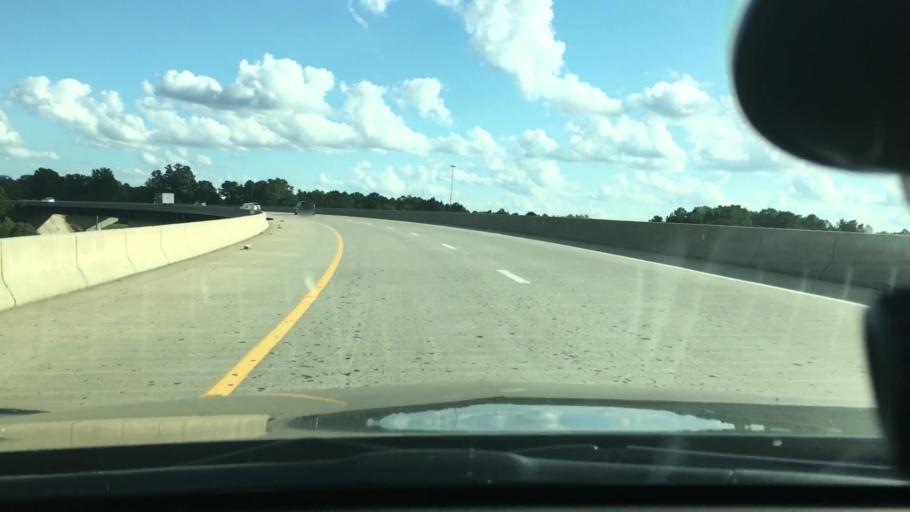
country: US
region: North Carolina
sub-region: Wake County
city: Raleigh
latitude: 35.7825
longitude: -78.5739
